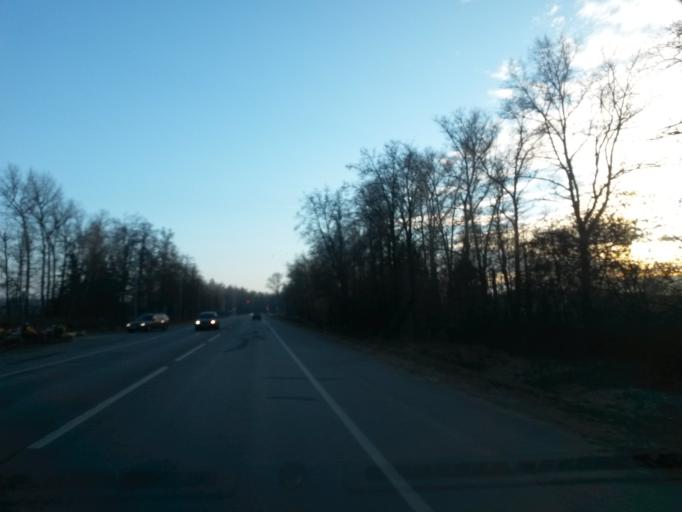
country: RU
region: Moskovskaya
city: Stolbovaya
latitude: 55.2601
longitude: 37.5092
